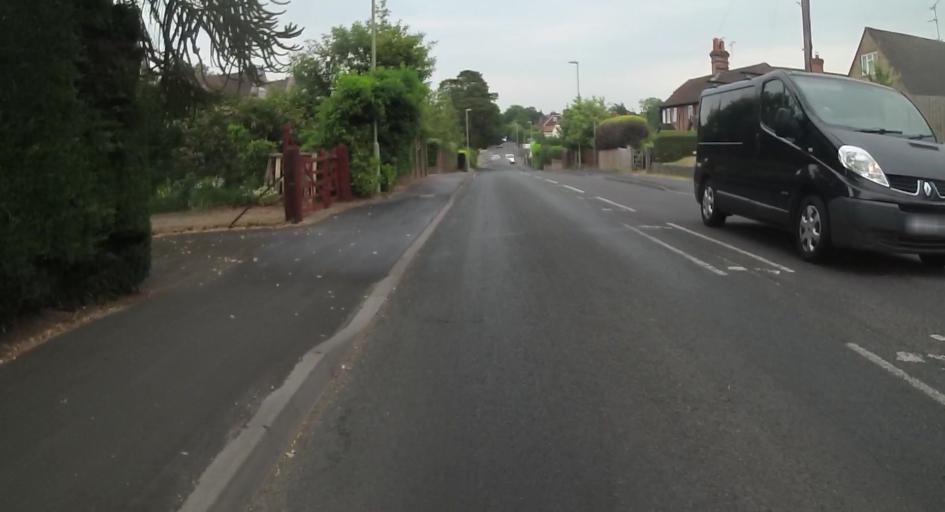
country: GB
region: England
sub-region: Hampshire
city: Fleet
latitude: 51.2596
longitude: -0.8393
